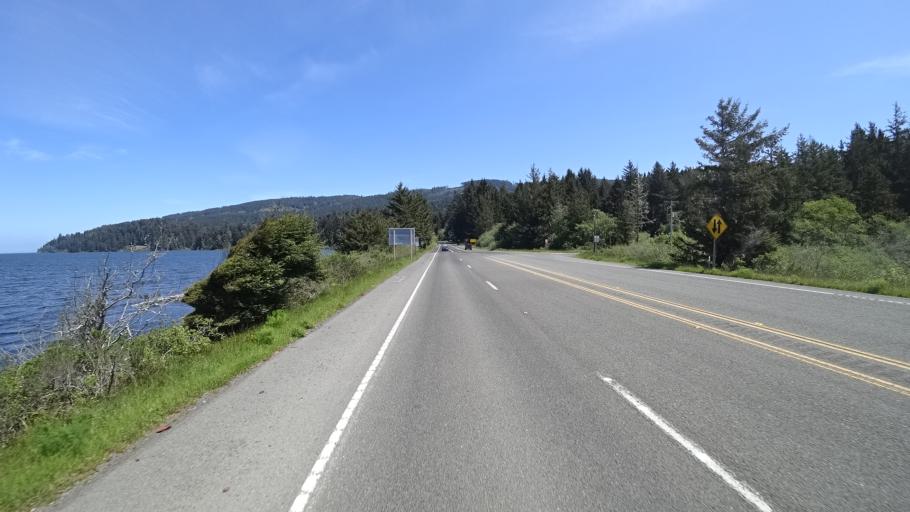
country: US
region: California
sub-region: Humboldt County
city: Westhaven-Moonstone
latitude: 41.1651
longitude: -124.1064
